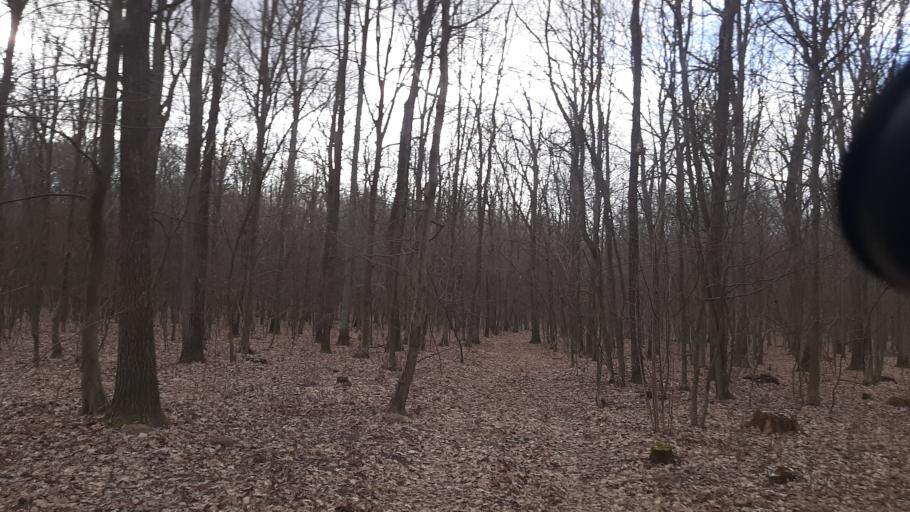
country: PL
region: Lublin Voivodeship
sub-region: Powiat lubelski
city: Jastkow
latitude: 51.3748
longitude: 22.4114
